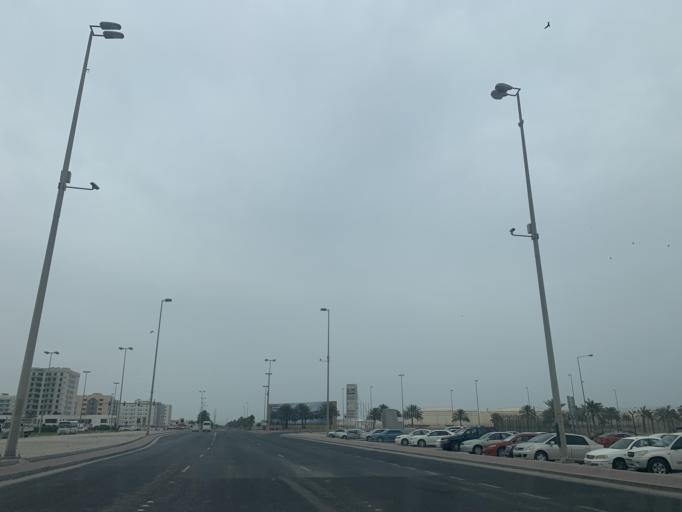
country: BH
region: Muharraq
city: Al Hadd
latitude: 26.2235
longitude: 50.6578
